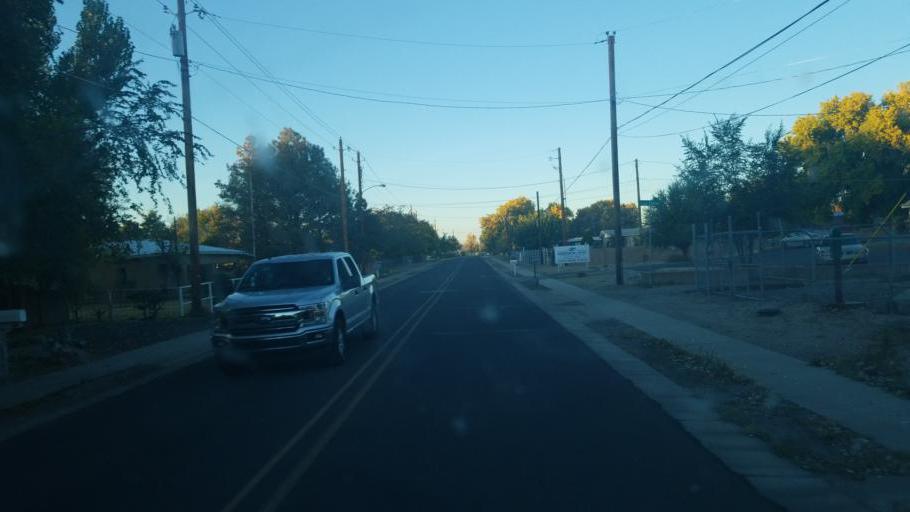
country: US
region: New Mexico
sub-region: Valencia County
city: Los Lunas
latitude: 34.8238
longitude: -106.7242
